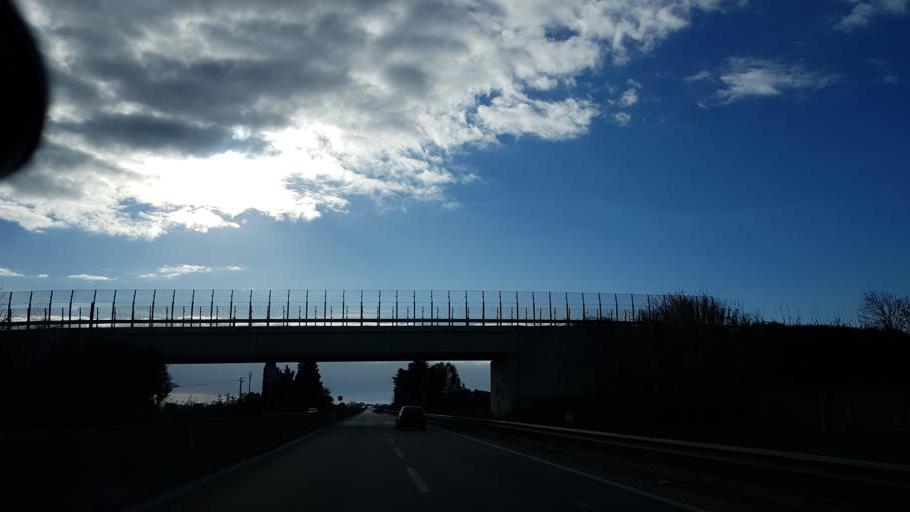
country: IT
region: Apulia
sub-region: Provincia di Brindisi
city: La Rosa
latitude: 40.5770
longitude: 17.9803
